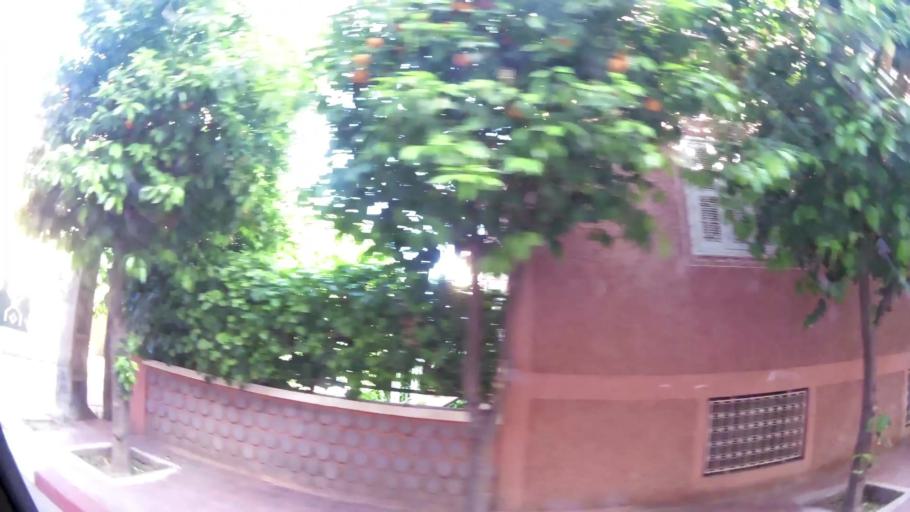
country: MA
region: Marrakech-Tensift-Al Haouz
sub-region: Marrakech
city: Marrakesh
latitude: 31.6553
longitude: -8.0067
